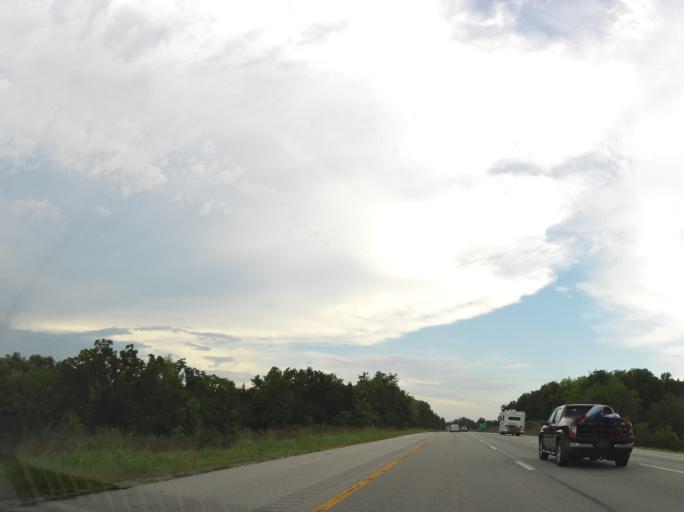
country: US
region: Kentucky
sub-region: Madison County
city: Berea
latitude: 37.6542
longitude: -84.3114
